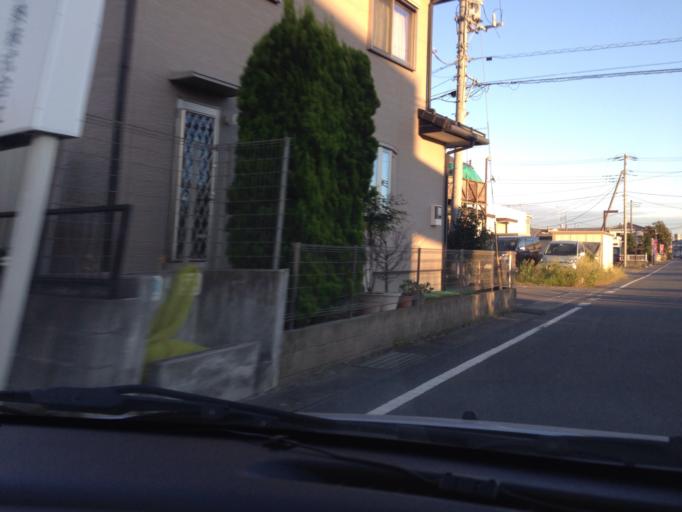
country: JP
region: Ibaraki
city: Naka
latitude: 36.0382
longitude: 140.1587
